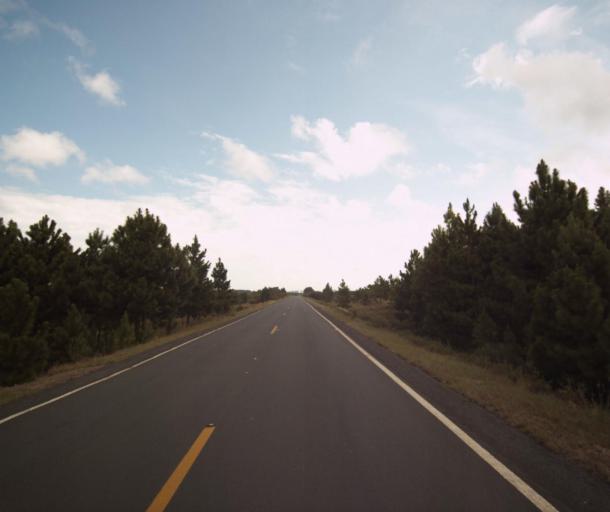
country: BR
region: Rio Grande do Sul
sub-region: Sao Lourenco Do Sul
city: Sao Lourenco do Sul
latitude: -31.4355
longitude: -51.1939
